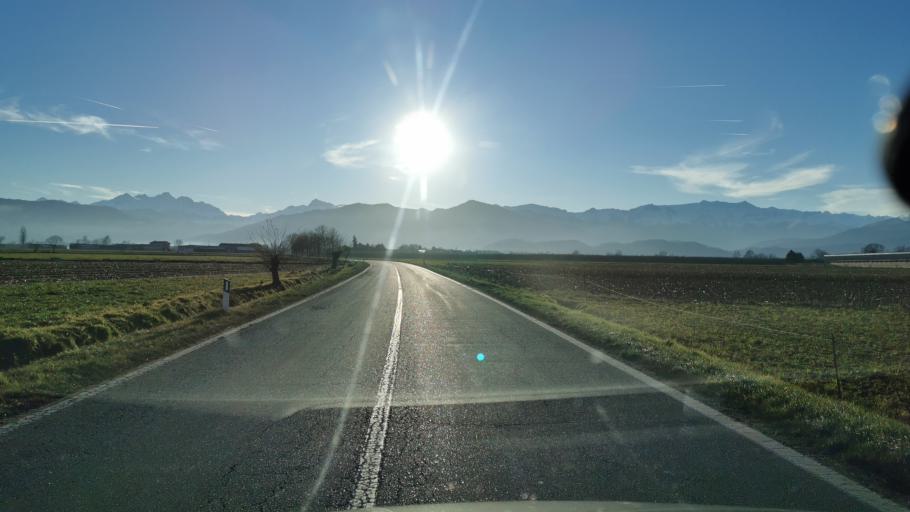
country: IT
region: Piedmont
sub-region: Provincia di Cuneo
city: Caraglio
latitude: 44.4455
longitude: 7.4711
